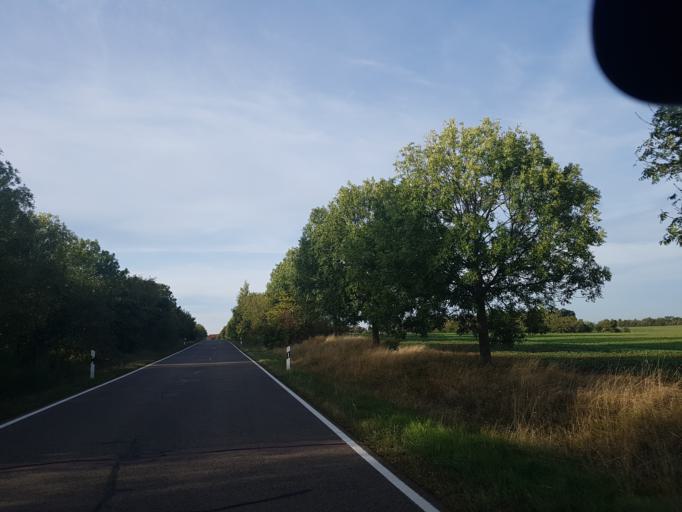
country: DE
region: Saxony
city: Waldheim
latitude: 51.0969
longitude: 13.0590
